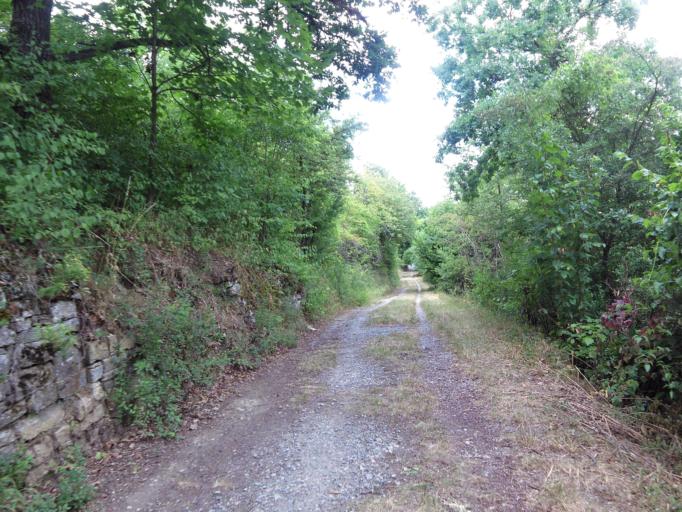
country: DE
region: Bavaria
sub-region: Regierungsbezirk Unterfranken
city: Gerbrunn
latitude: 49.7756
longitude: 9.9927
